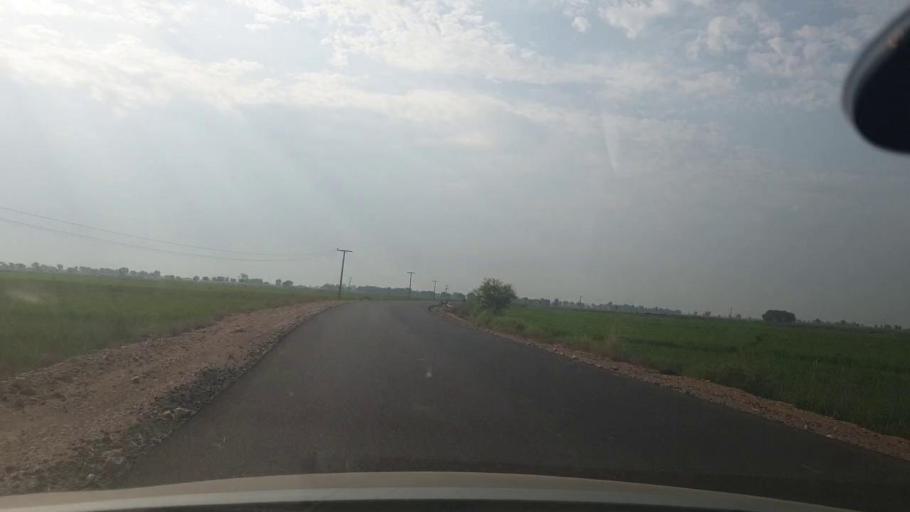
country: PK
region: Sindh
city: Jacobabad
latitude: 28.0987
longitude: 68.3283
